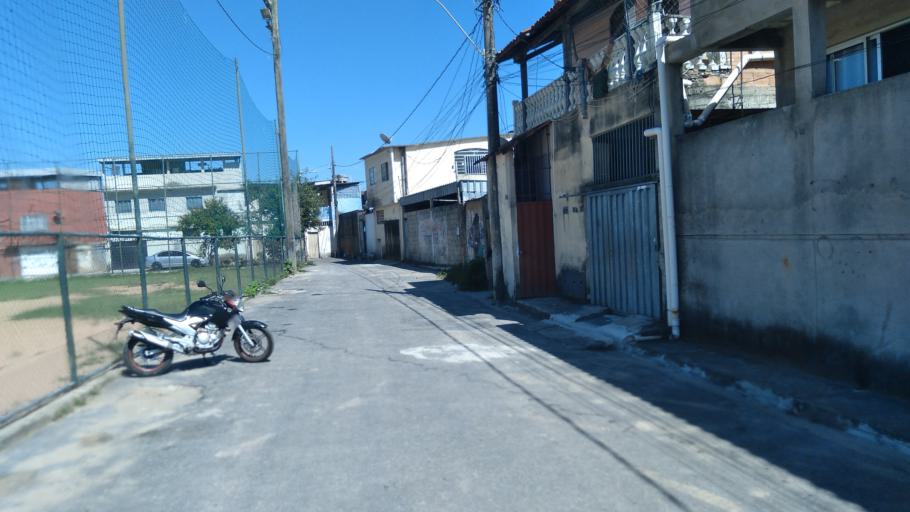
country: BR
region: Minas Gerais
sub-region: Belo Horizonte
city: Belo Horizonte
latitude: -19.8658
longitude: -43.9234
